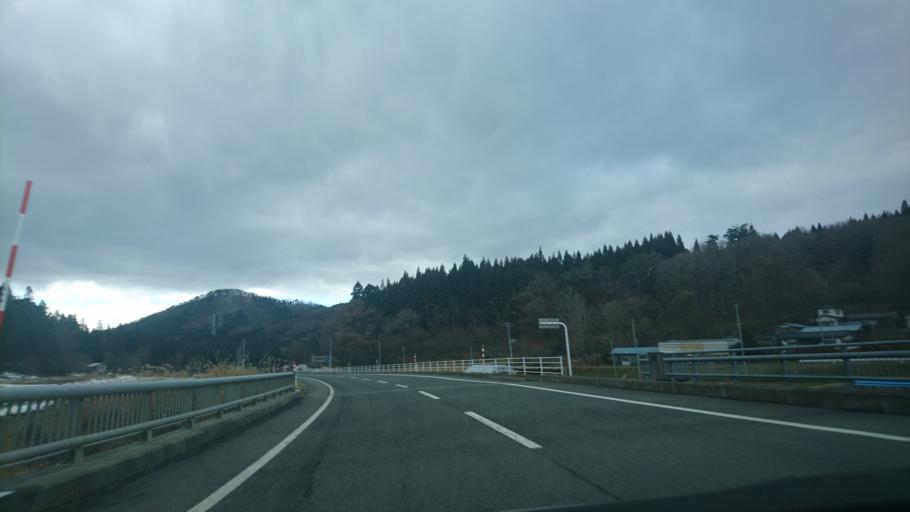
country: JP
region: Iwate
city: Mizusawa
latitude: 39.1808
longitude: 141.3001
